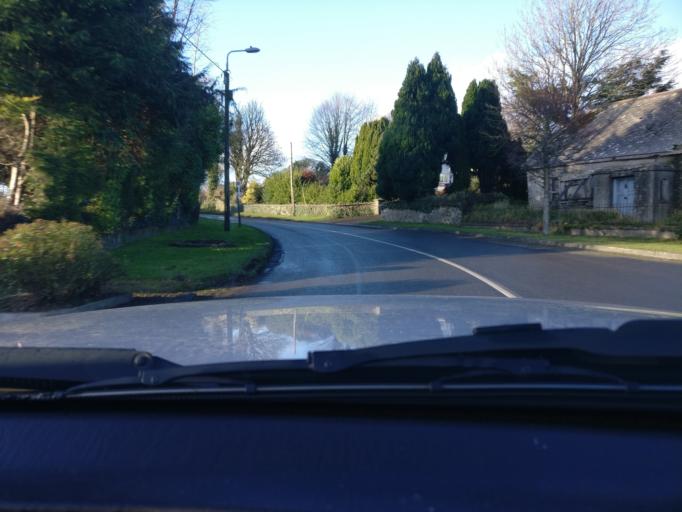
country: IE
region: Leinster
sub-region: An Mhi
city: Athboy
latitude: 53.6931
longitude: -6.9969
